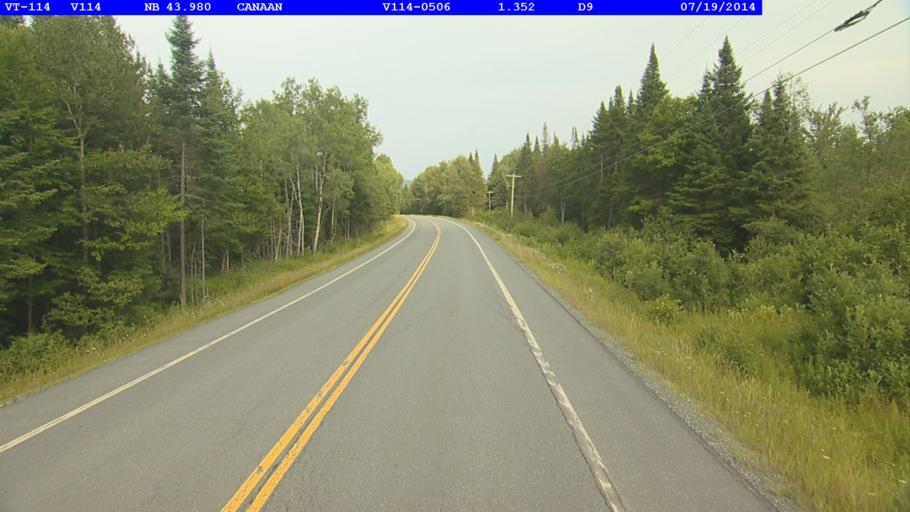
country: CA
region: Quebec
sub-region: Estrie
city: Coaticook
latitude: 45.0059
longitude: -71.6664
